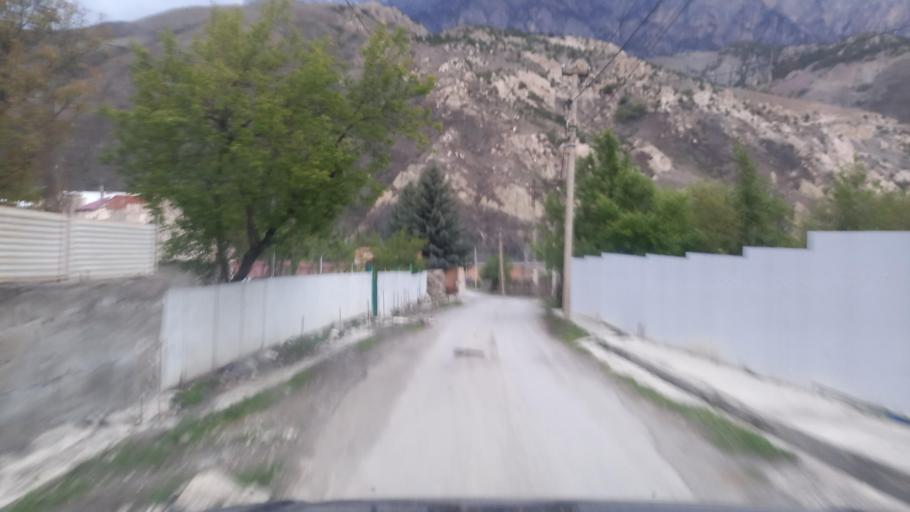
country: RU
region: North Ossetia
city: Mizur
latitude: 42.8598
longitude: 44.1466
